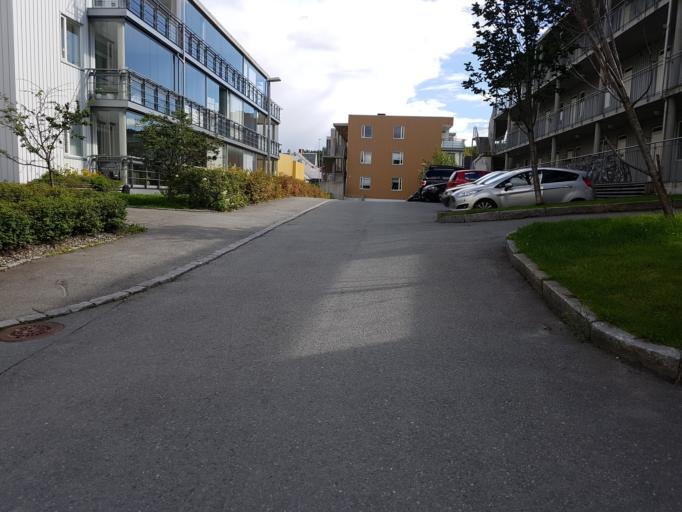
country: NO
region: Sor-Trondelag
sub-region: Trondheim
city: Trondheim
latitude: 63.4135
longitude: 10.4713
